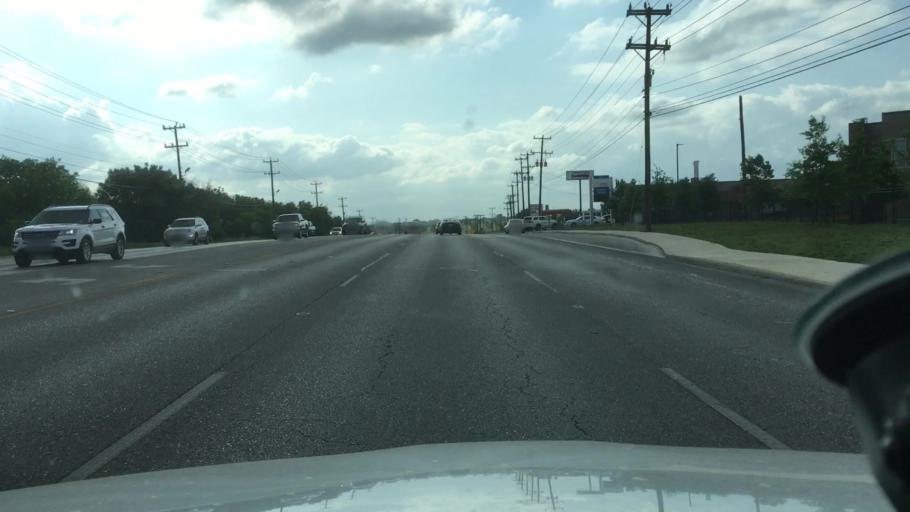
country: US
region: Texas
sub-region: Bexar County
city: Windcrest
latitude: 29.5022
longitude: -98.3618
